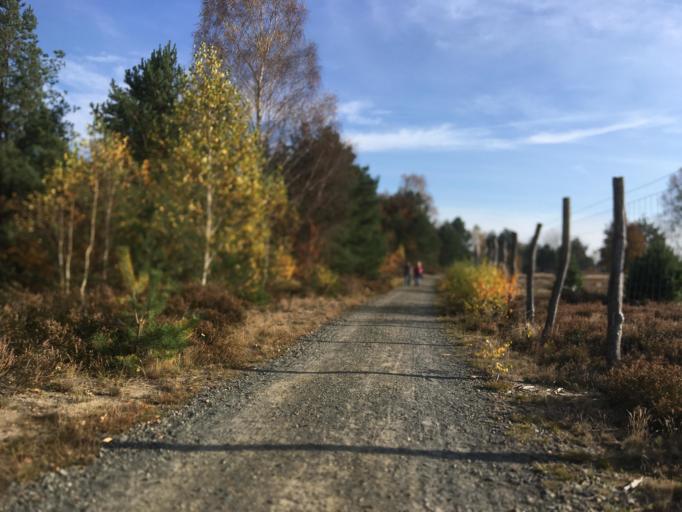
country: DE
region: Berlin
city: Buch
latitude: 52.6937
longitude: 13.5076
